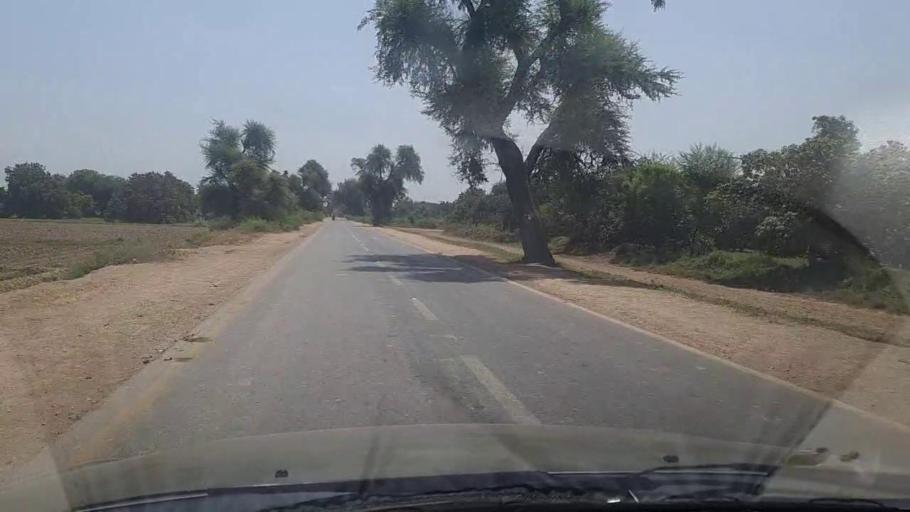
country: PK
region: Sindh
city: Tando Jam
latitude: 25.3322
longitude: 68.5379
